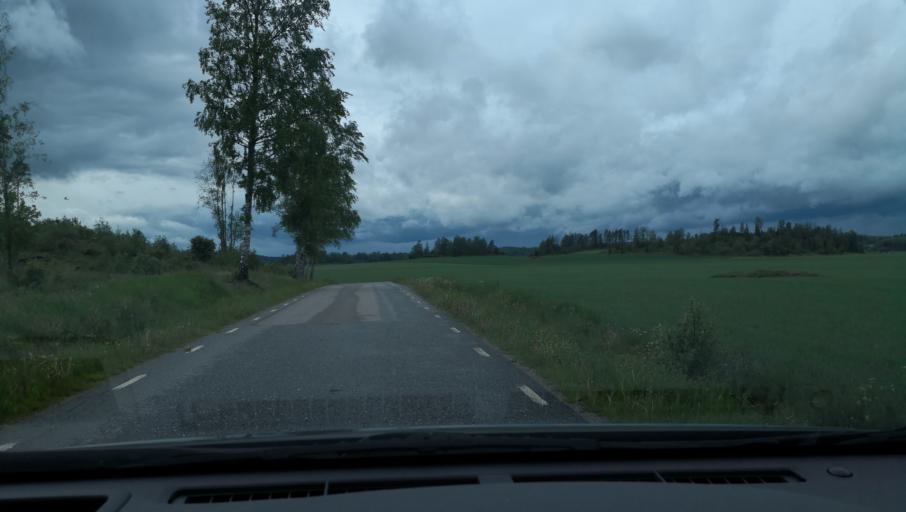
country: SE
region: Uppsala
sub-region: Enkopings Kommun
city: Orsundsbro
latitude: 59.7257
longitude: 17.3748
